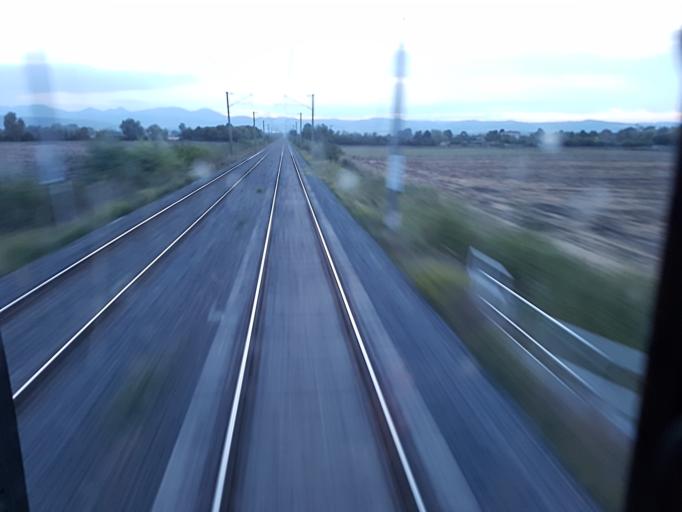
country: FR
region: Auvergne
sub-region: Departement du Puy-de-Dome
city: Ennezat
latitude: 45.9069
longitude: 3.1863
